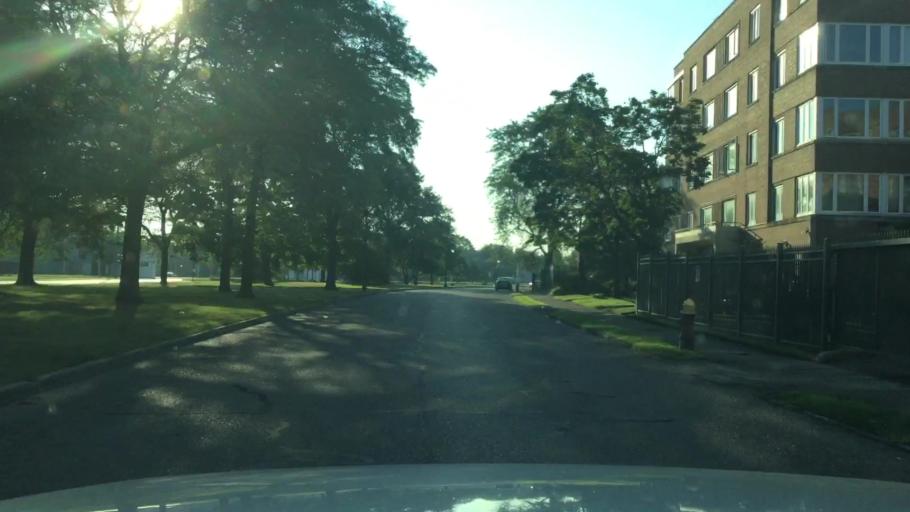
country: US
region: Michigan
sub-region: Wayne County
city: Highland Park
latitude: 42.4190
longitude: -83.1102
